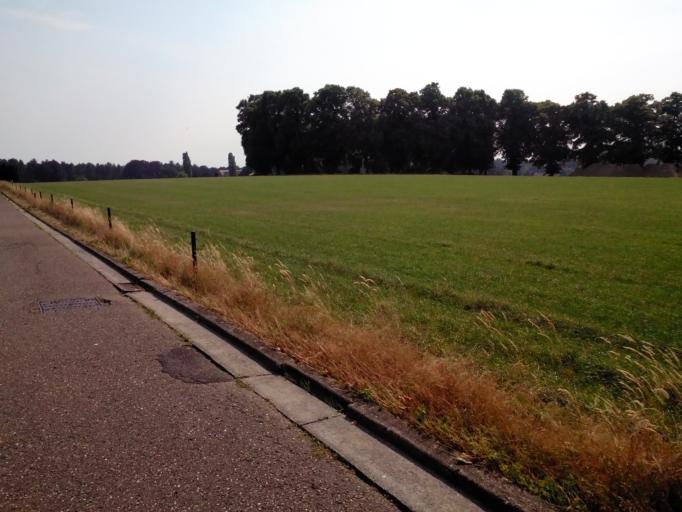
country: BE
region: Flanders
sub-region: Provincie Vlaams-Brabant
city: Leuven
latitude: 50.8530
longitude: 4.7042
